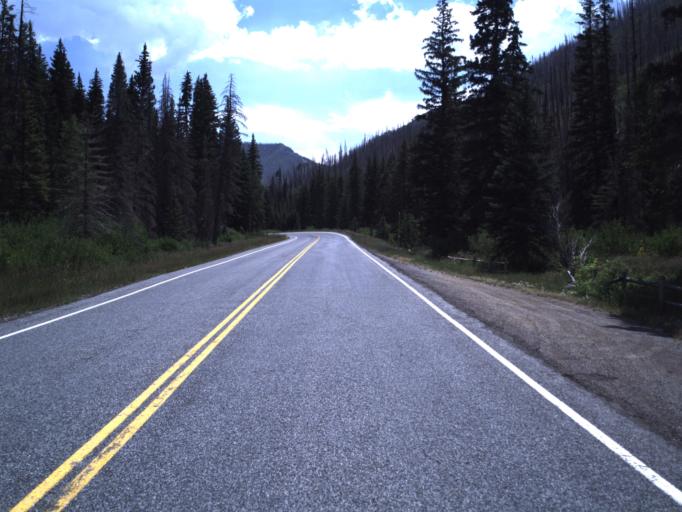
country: US
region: Utah
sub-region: Sanpete County
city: Fairview
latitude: 39.5530
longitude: -111.1706
